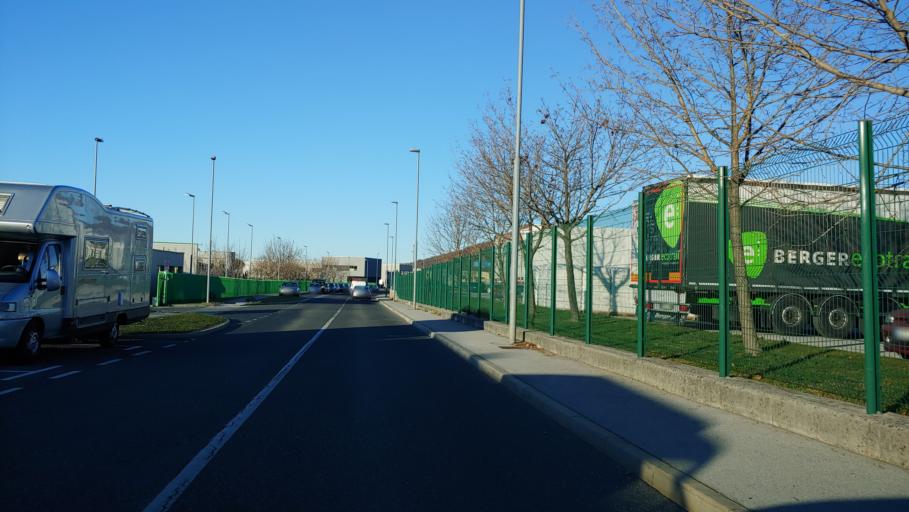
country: SI
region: Sezana
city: Sezana
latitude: 45.7088
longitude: 13.8598
